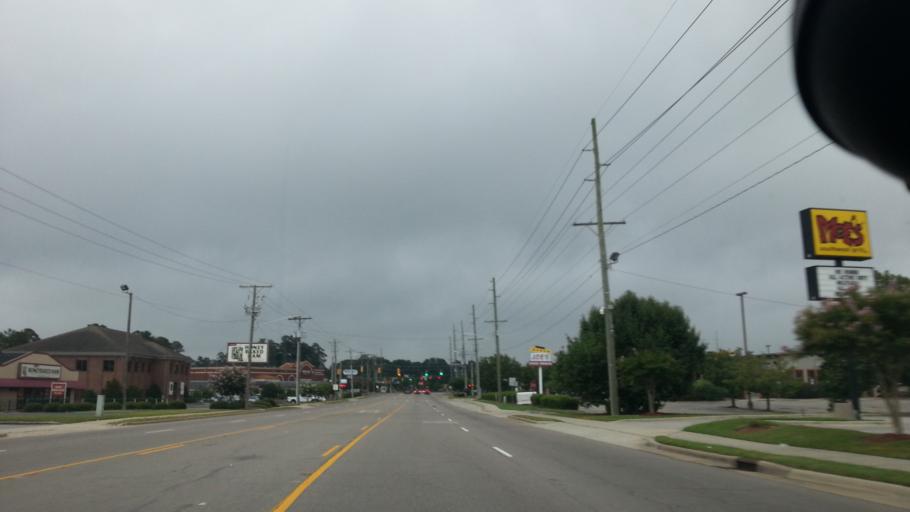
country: US
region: North Carolina
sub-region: Cumberland County
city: Fayetteville
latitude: 35.0701
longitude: -78.9514
